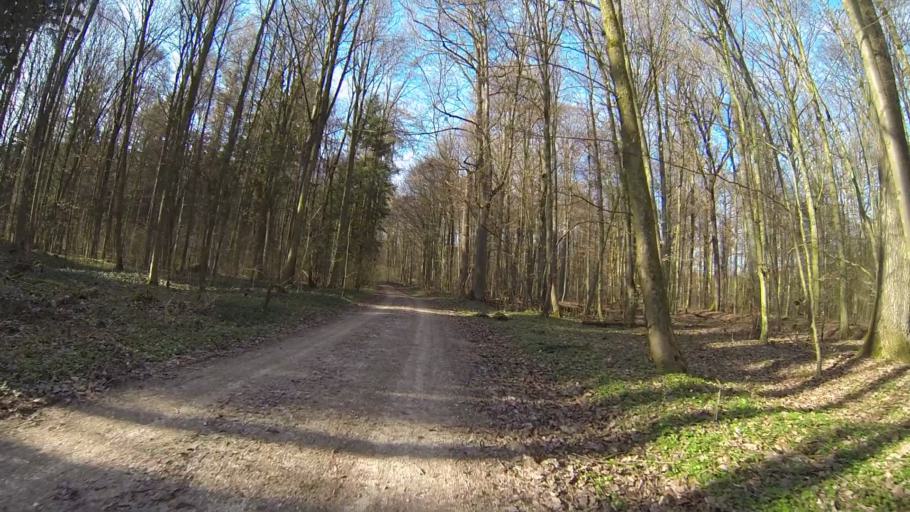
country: DE
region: Baden-Wuerttemberg
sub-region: Regierungsbezirk Stuttgart
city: Niederstotzingen
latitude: 48.5559
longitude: 10.2309
